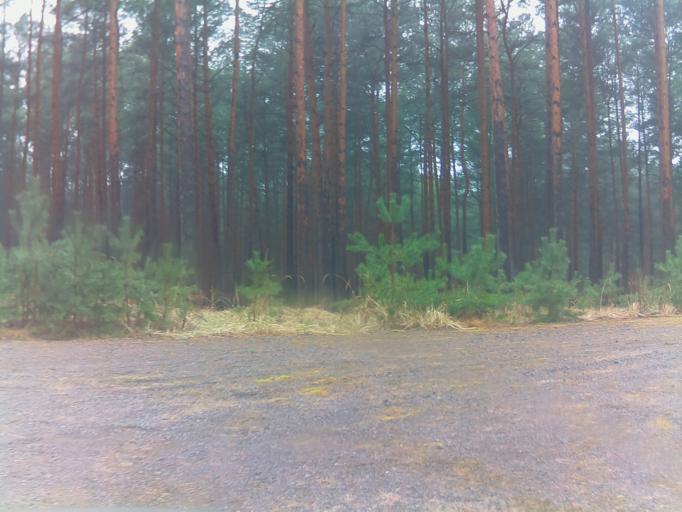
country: DE
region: Brandenburg
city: Jamlitz
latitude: 52.0518
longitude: 14.3658
